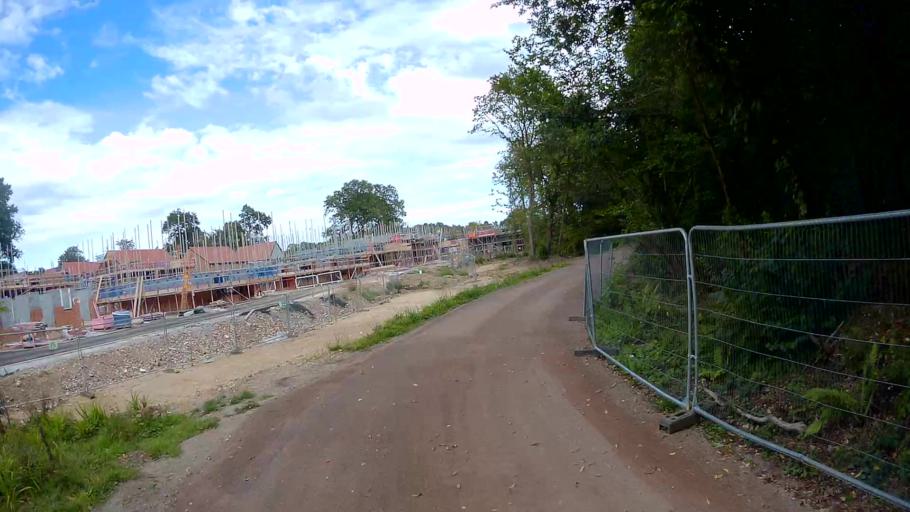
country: GB
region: England
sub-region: Surrey
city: Frimley
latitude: 51.3028
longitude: -0.7073
